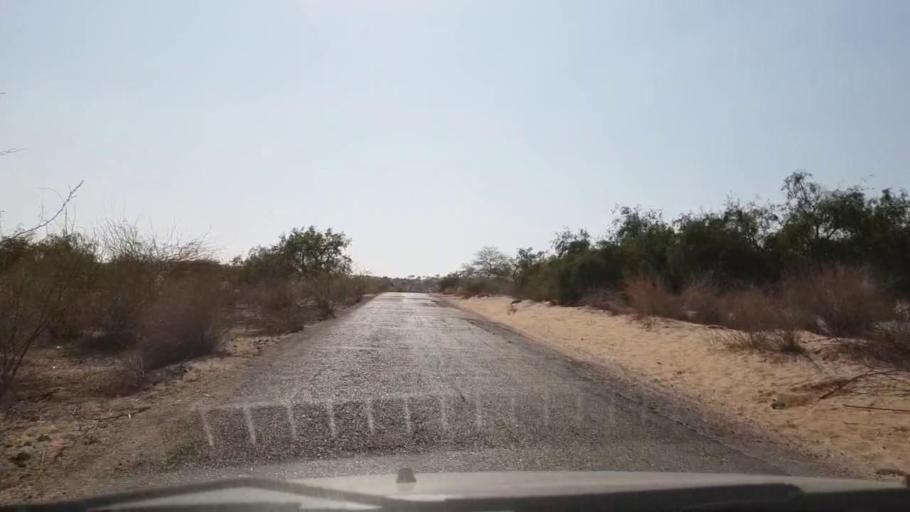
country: PK
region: Sindh
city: Mithi
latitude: 24.6377
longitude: 69.7431
